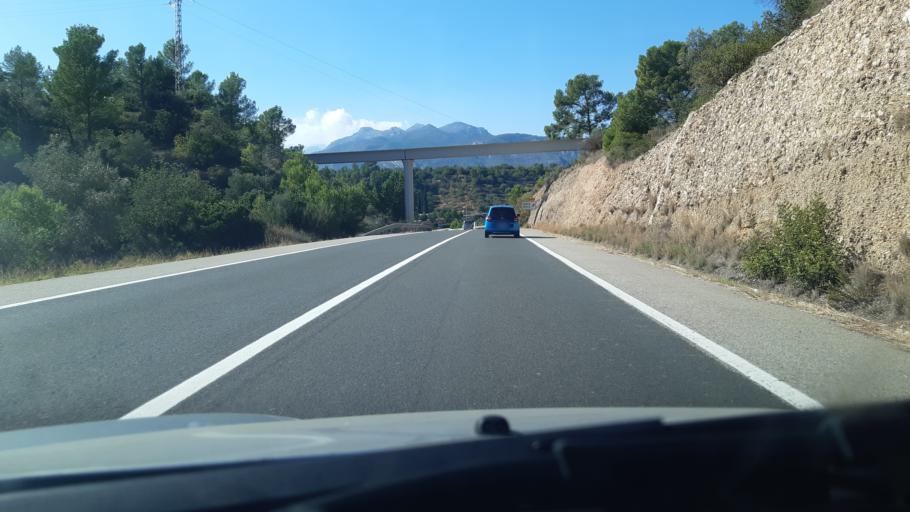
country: ES
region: Catalonia
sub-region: Provincia de Tarragona
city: Tivenys
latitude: 40.9140
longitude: 0.4897
